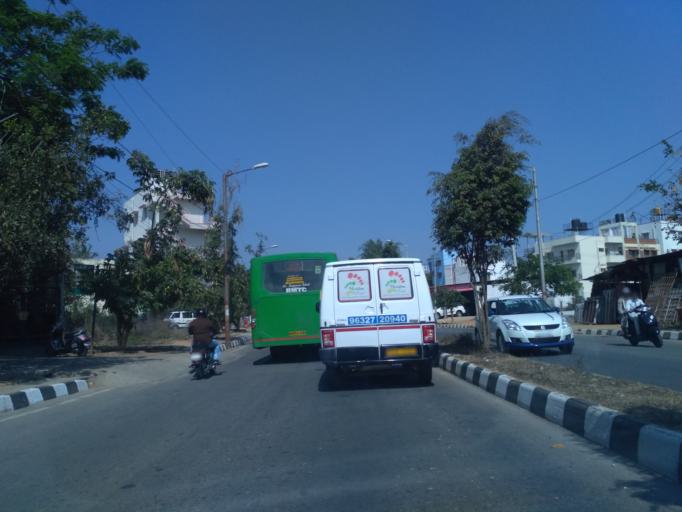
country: IN
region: Karnataka
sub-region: Bangalore Urban
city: Yelahanka
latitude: 13.0833
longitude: 77.5510
